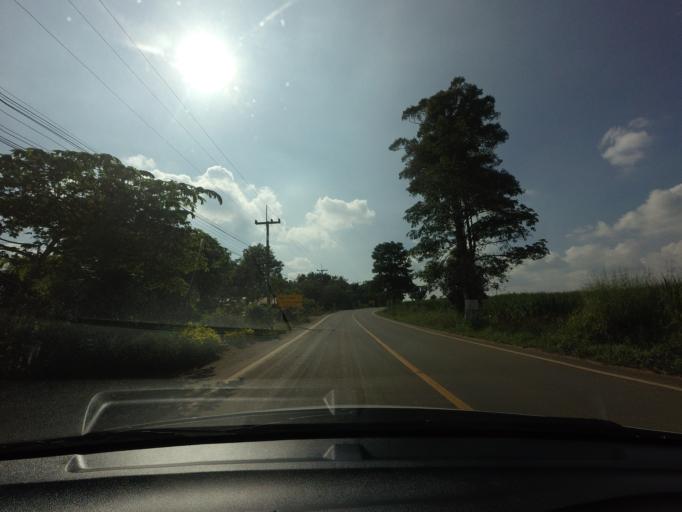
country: TH
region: Nakhon Ratchasima
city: Wang Nam Khiao
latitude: 14.4684
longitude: 101.6290
